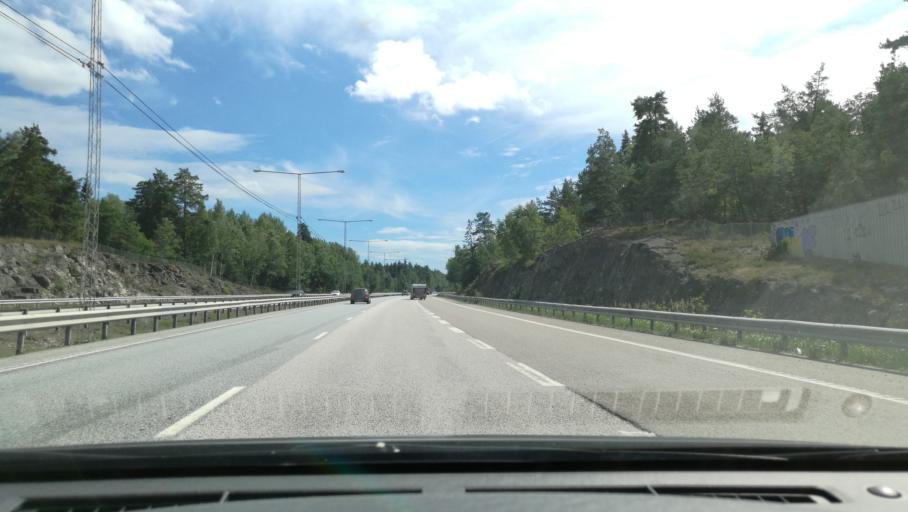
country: SE
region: Stockholm
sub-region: Jarfalla Kommun
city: Jakobsberg
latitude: 59.4477
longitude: 17.8396
